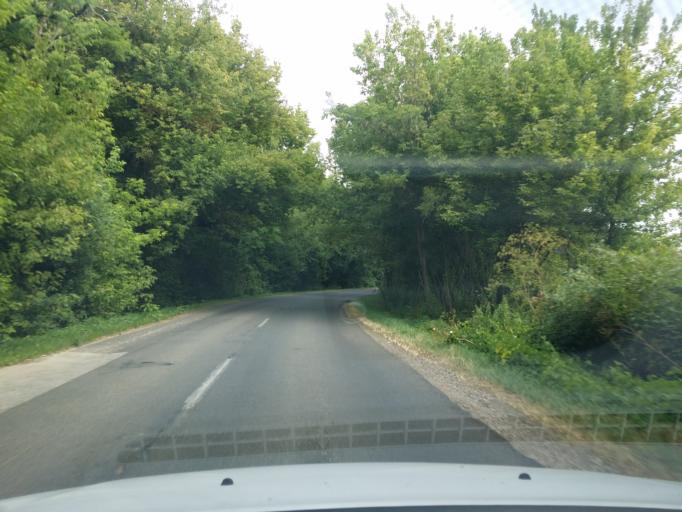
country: HU
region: Pest
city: Acsa
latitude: 47.8106
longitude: 19.3880
